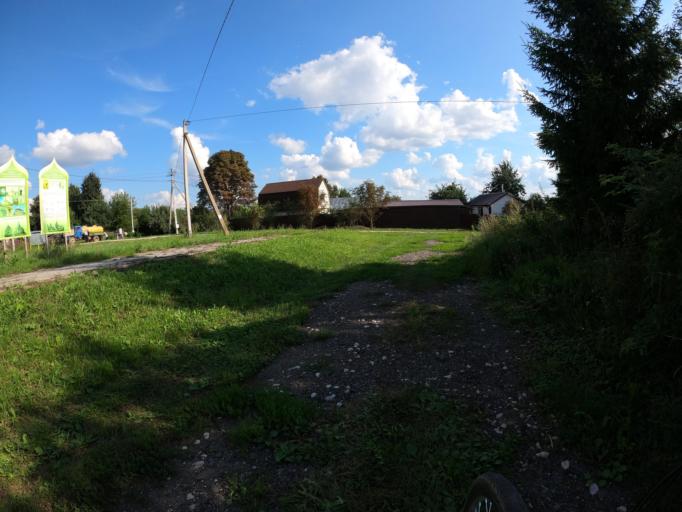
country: RU
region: Moskovskaya
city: Troitskoye
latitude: 55.2132
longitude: 38.4875
